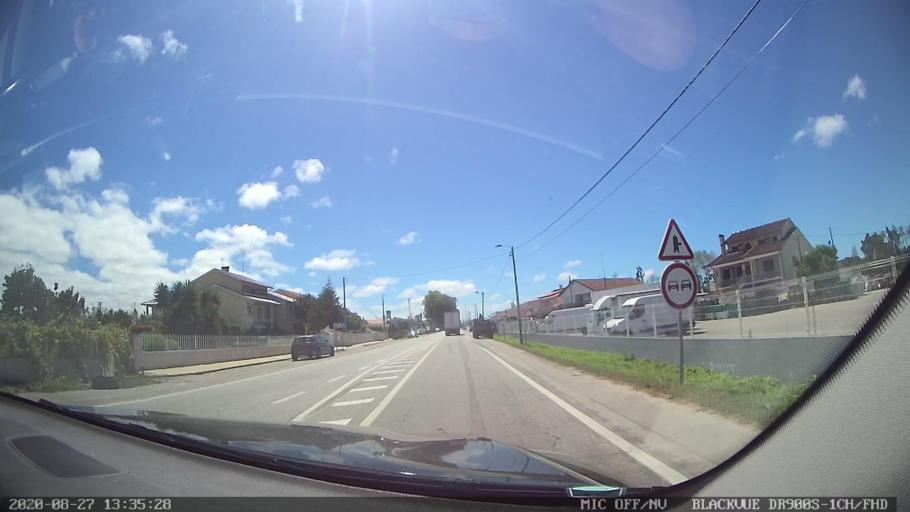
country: PT
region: Coimbra
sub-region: Mira
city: Mira
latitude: 40.4633
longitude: -8.7005
